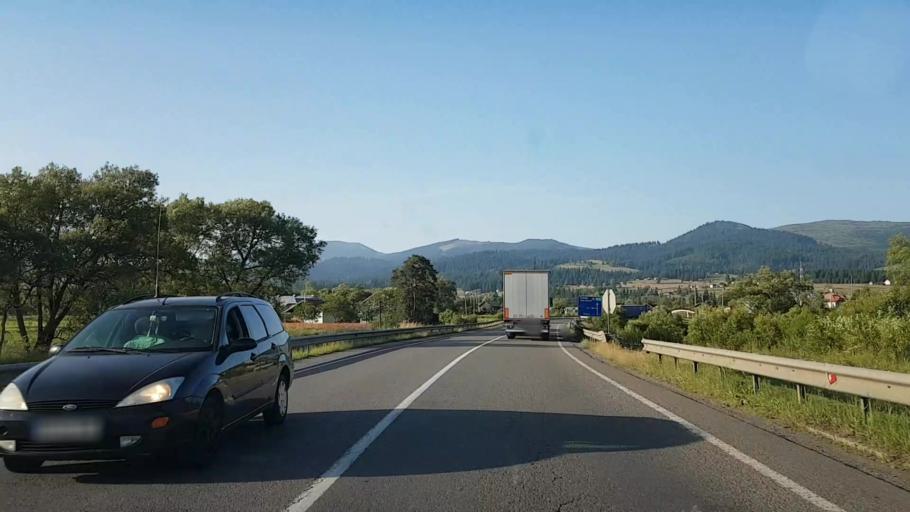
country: RO
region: Suceava
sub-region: Comuna Cosna
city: Cosna
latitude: 47.3591
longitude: 25.1893
